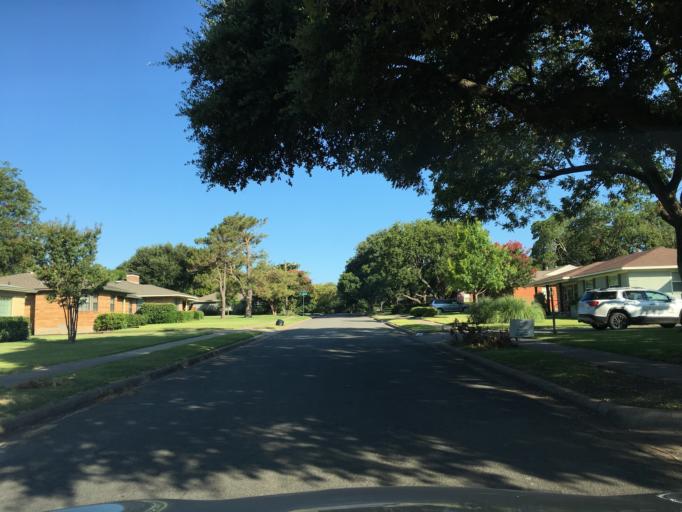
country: US
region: Texas
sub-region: Dallas County
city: Garland
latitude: 32.8585
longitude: -96.7078
